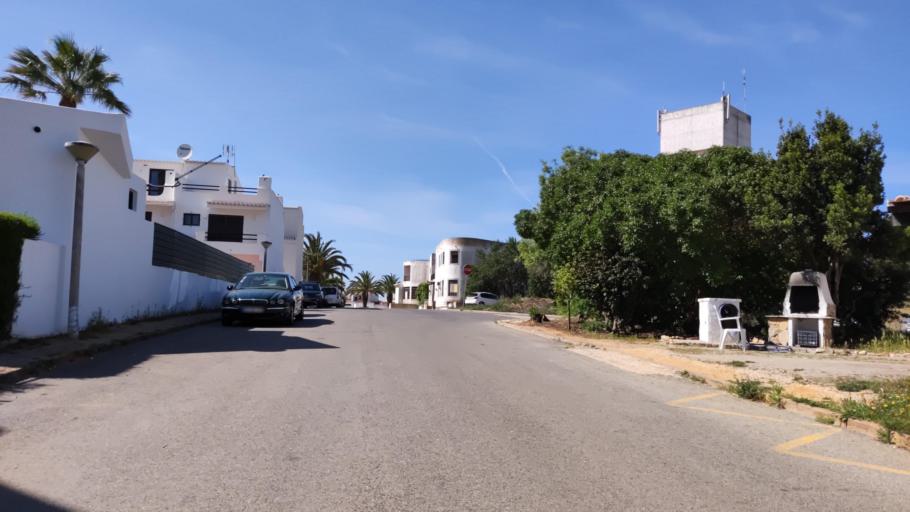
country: PT
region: Faro
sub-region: Lagos
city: Lagos
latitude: 37.0939
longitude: -8.6823
